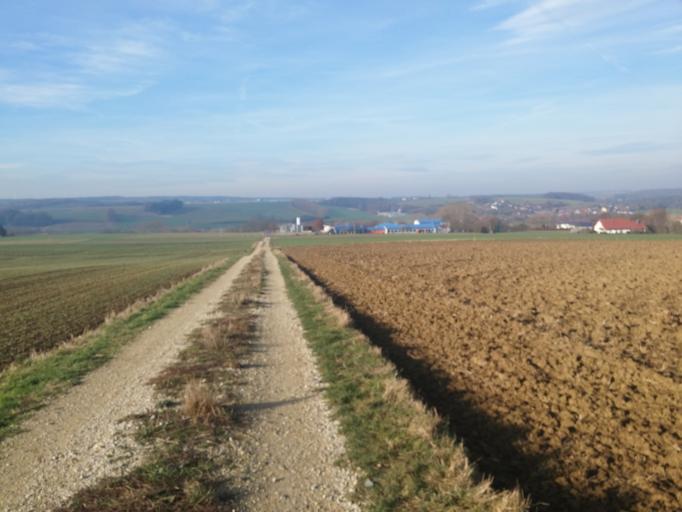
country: DE
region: Bavaria
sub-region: Upper Franconia
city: Grossheirath
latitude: 50.1673
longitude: 10.9507
